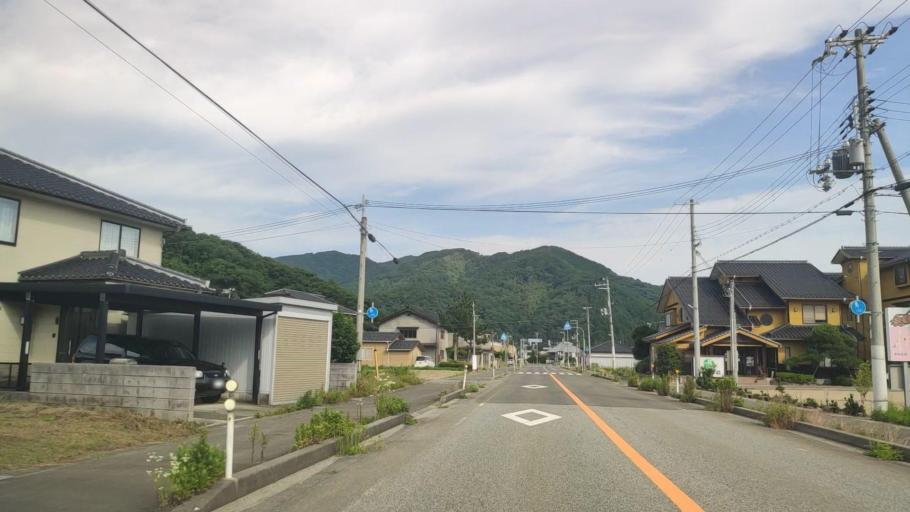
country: JP
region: Hyogo
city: Toyooka
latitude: 35.6414
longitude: 134.8346
